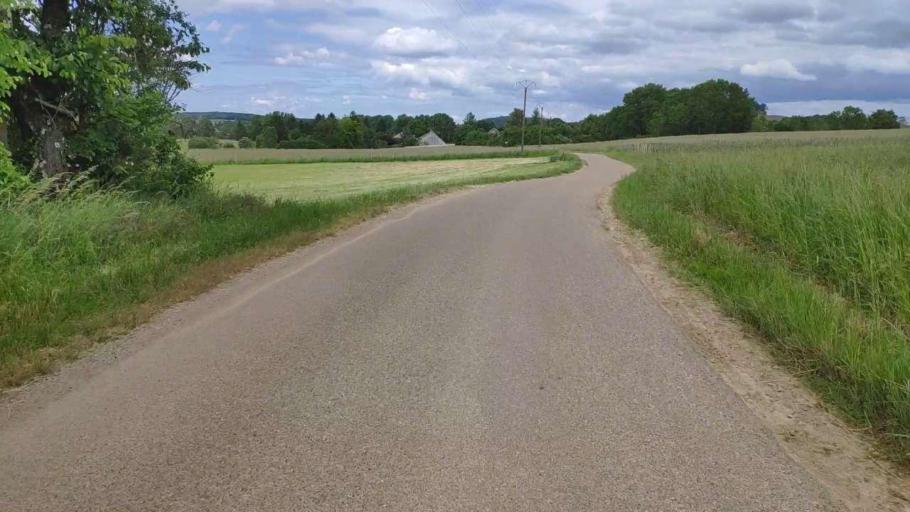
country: FR
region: Franche-Comte
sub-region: Departement du Jura
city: Bletterans
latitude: 46.7468
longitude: 5.5190
